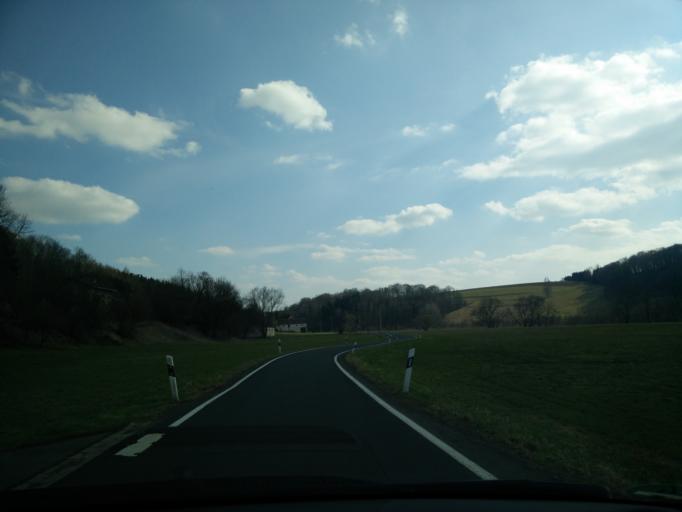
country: DE
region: Saxony
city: Colditz
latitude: 51.0995
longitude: 12.8062
